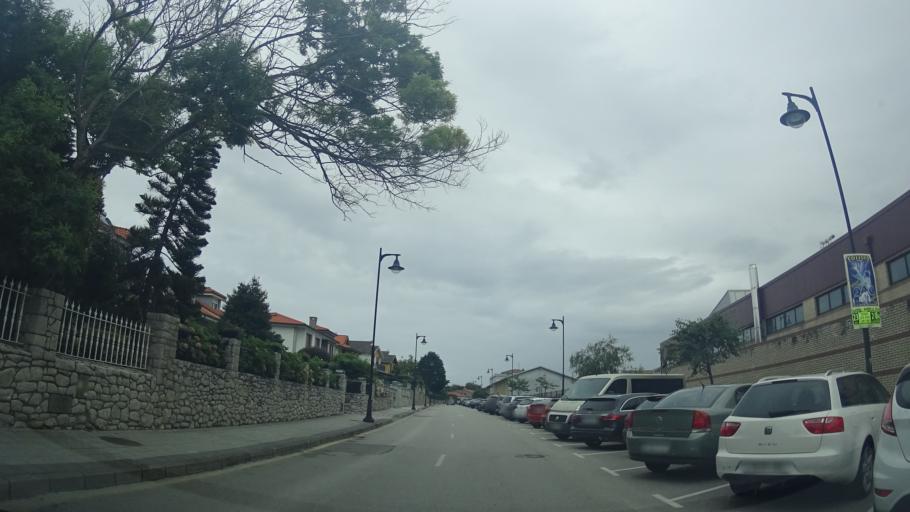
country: ES
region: Asturias
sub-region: Province of Asturias
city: Llanes
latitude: 43.4246
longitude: -4.7617
